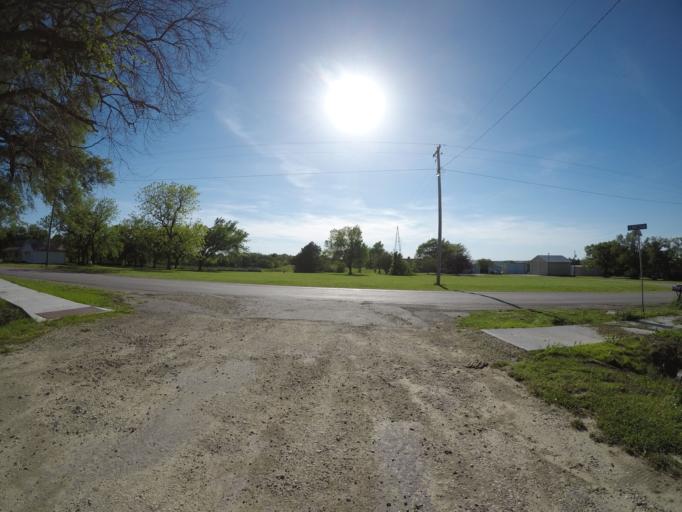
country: US
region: Kansas
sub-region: Clay County
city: Clay Center
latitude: 39.4334
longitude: -96.9981
